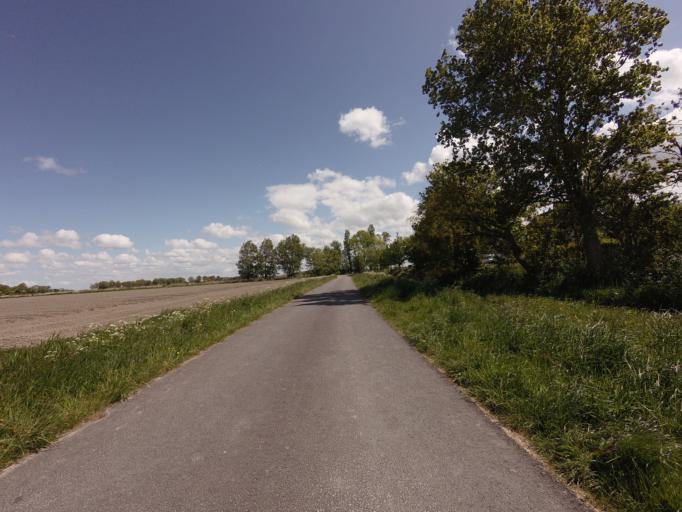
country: NL
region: Friesland
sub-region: Gemeente Harlingen
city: Harlingen
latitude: 53.1371
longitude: 5.4335
